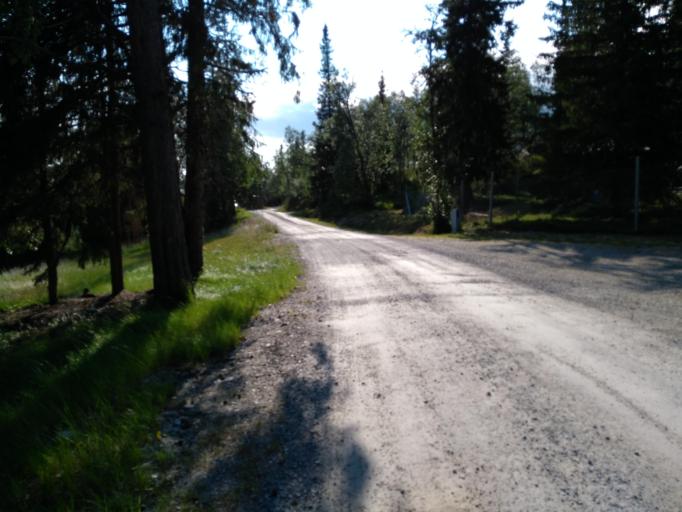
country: SE
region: Jaemtland
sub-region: Are Kommun
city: Are
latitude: 62.6617
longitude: 12.8766
